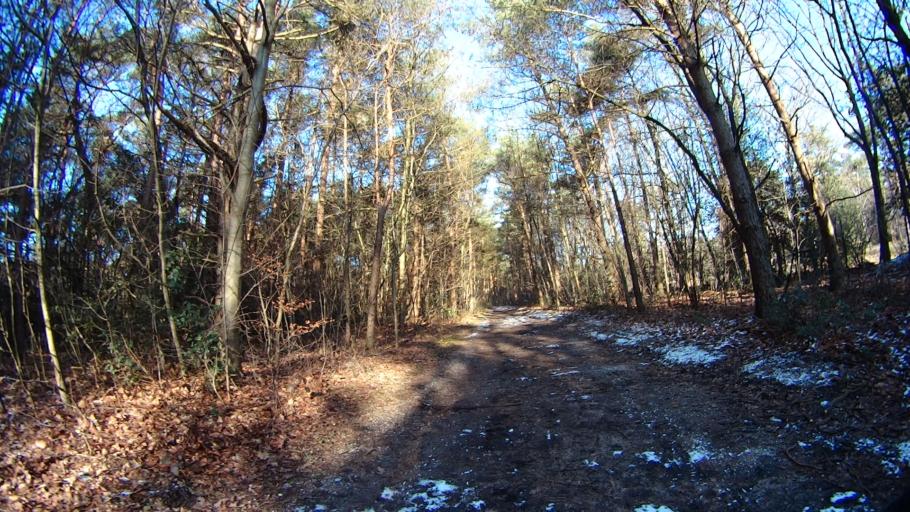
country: NL
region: North Holland
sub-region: Gemeente Laren
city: Laren
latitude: 52.2587
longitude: 5.2031
